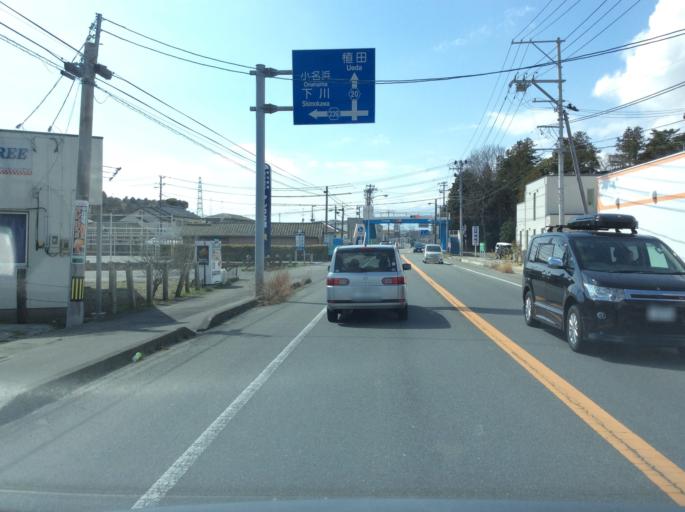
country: JP
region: Fukushima
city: Iwaki
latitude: 36.9473
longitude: 140.8596
